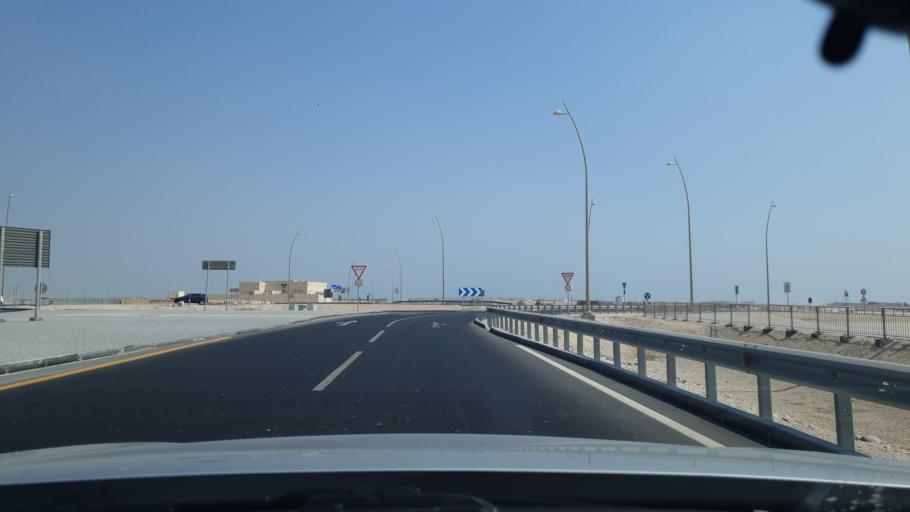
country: QA
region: Al Khawr
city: Al Khawr
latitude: 25.6661
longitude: 51.5153
